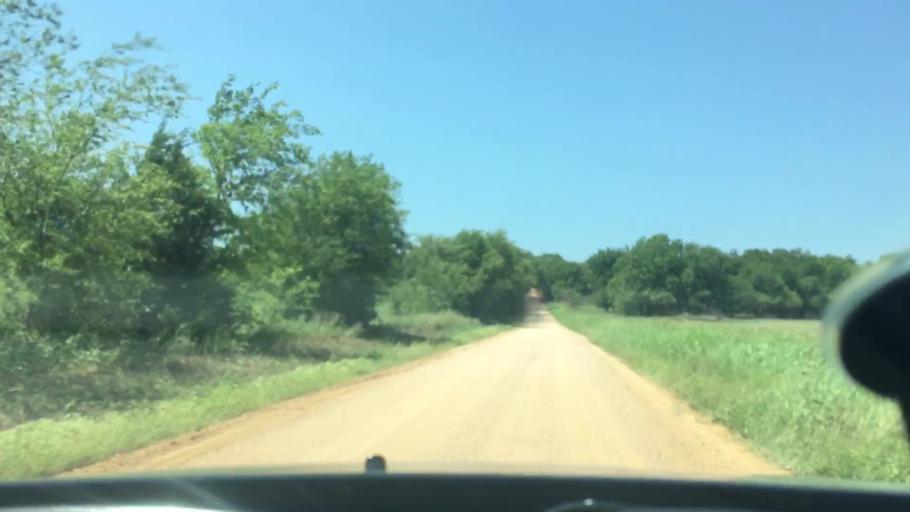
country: US
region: Oklahoma
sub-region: Johnston County
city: Tishomingo
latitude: 34.3459
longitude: -96.4283
